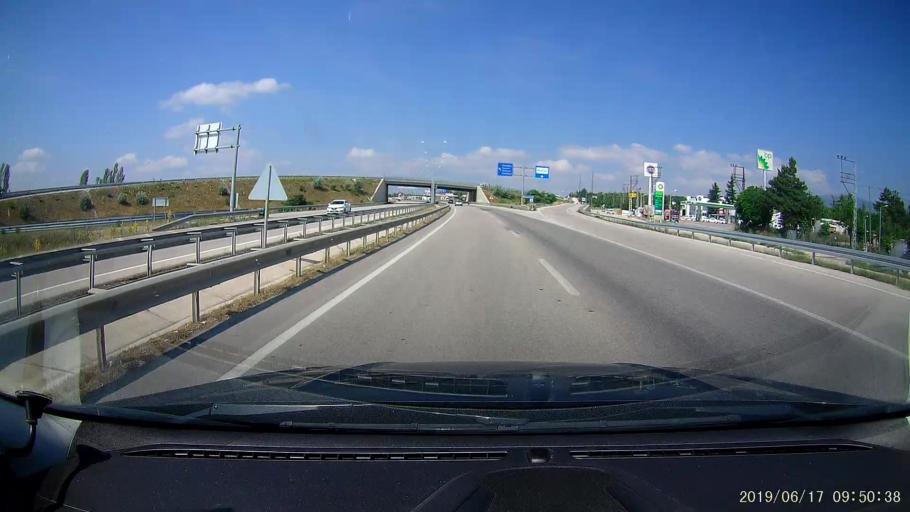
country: TR
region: Amasya
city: Merzifon
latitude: 40.8704
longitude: 35.5023
